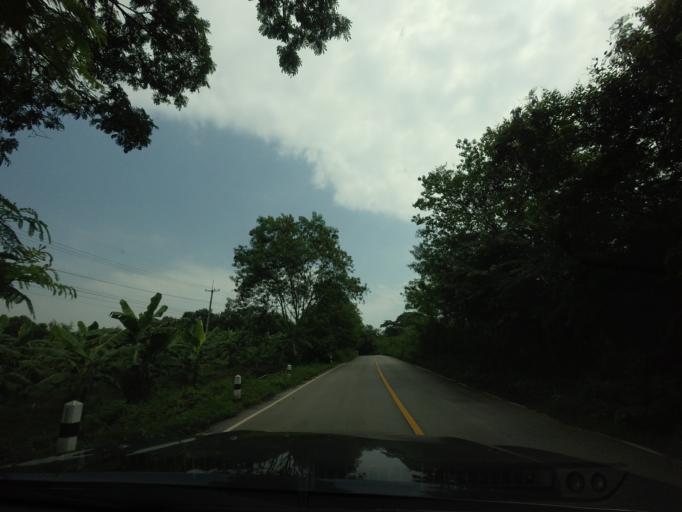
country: TH
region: Loei
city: Tha Li
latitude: 17.6497
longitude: 101.3828
